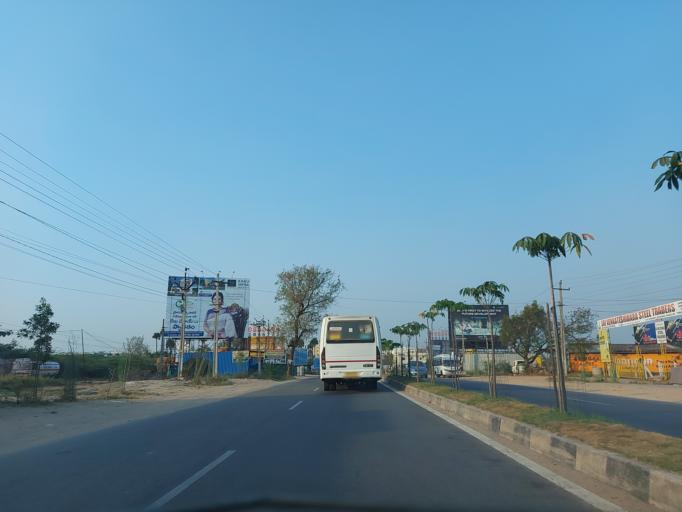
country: IN
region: Telangana
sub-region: Rangareddi
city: Balapur
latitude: 17.2008
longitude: 78.4760
